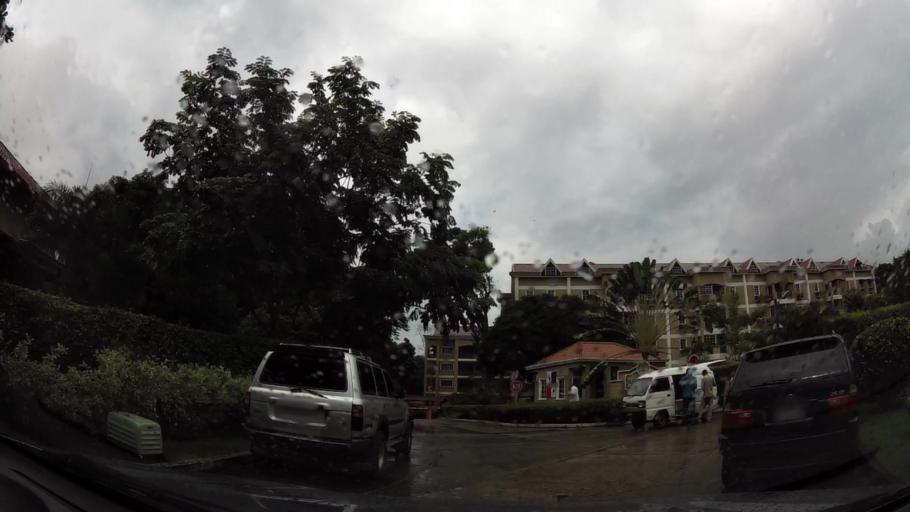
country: PA
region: Panama
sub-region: Distrito de Panama
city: Ancon
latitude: 8.9808
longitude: -79.5587
